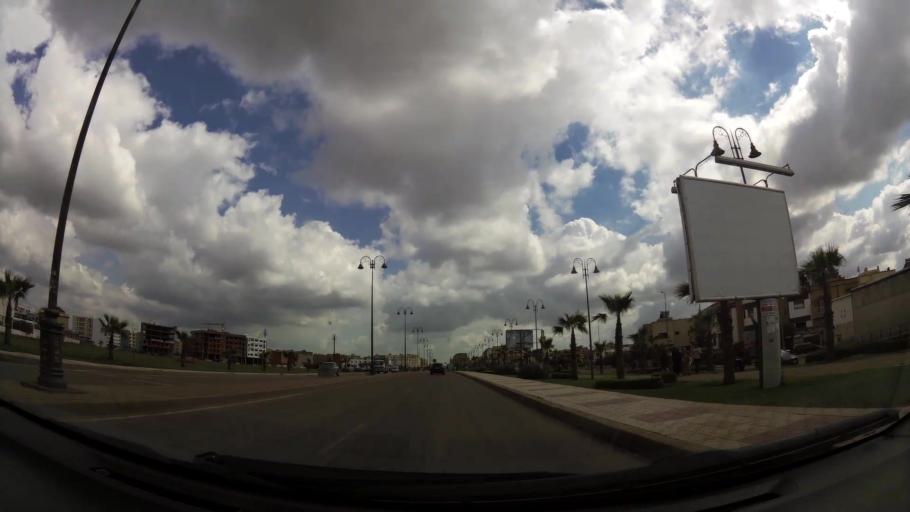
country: MA
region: Chaouia-Ouardigha
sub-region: Settat Province
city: Berrechid
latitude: 33.2795
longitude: -7.5899
